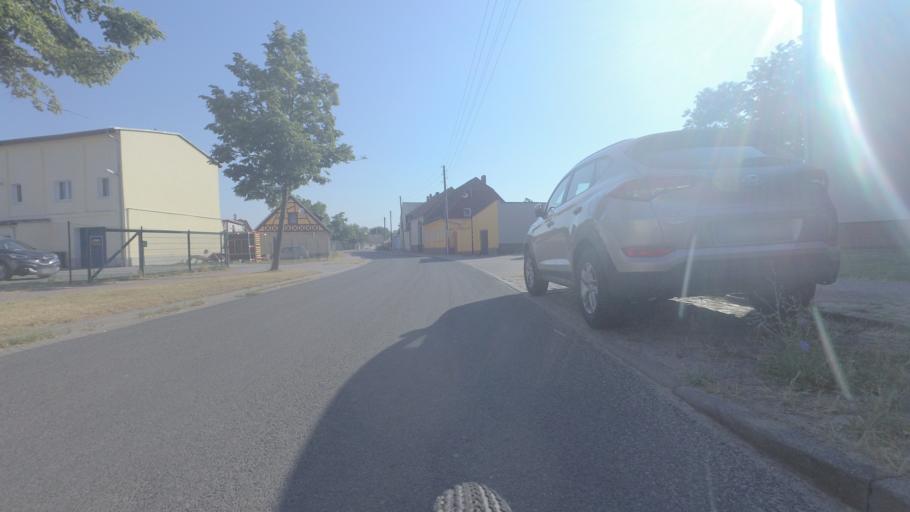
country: DE
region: Saxony-Anhalt
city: Osternienburg
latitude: 51.7931
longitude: 12.0283
